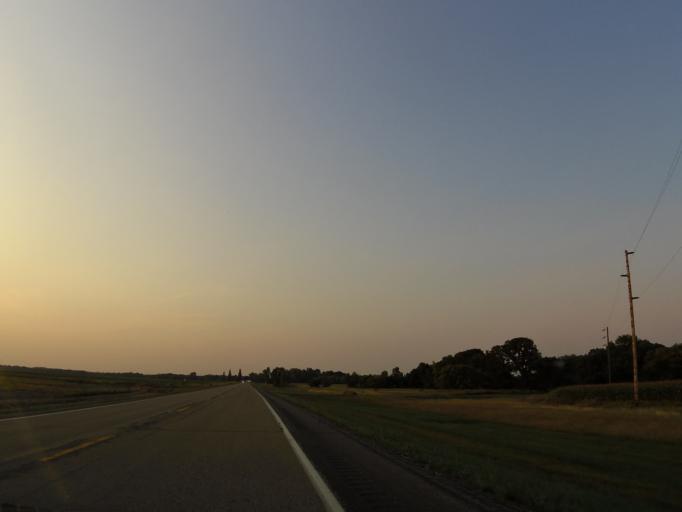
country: US
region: North Dakota
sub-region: Grand Forks County
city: Larimore
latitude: 47.9825
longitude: -97.6240
